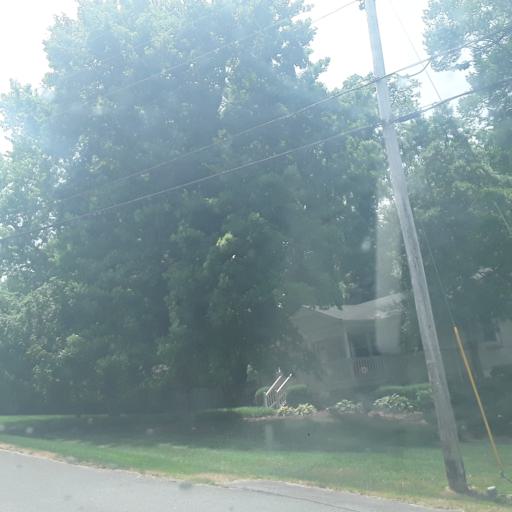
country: US
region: Tennessee
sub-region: Williamson County
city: Brentwood
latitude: 36.0596
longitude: -86.7577
